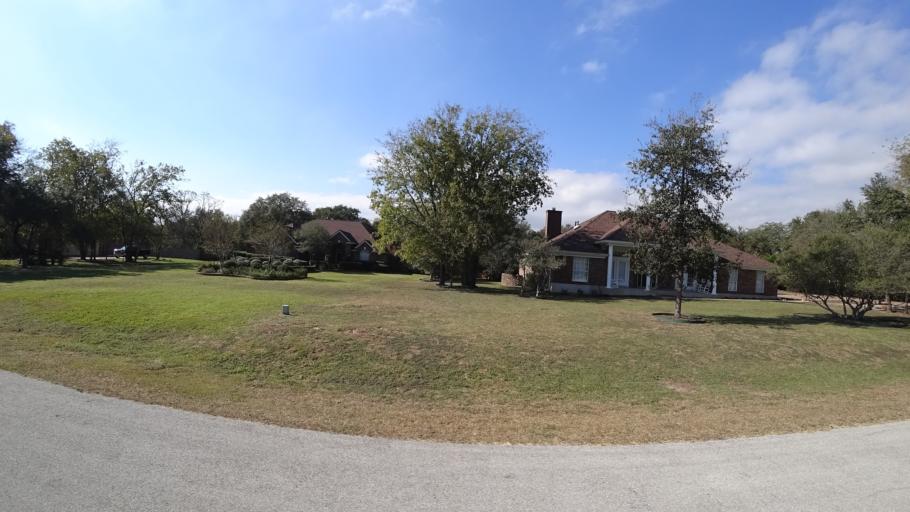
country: US
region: Texas
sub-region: Travis County
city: Shady Hollow
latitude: 30.1605
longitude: -97.8704
